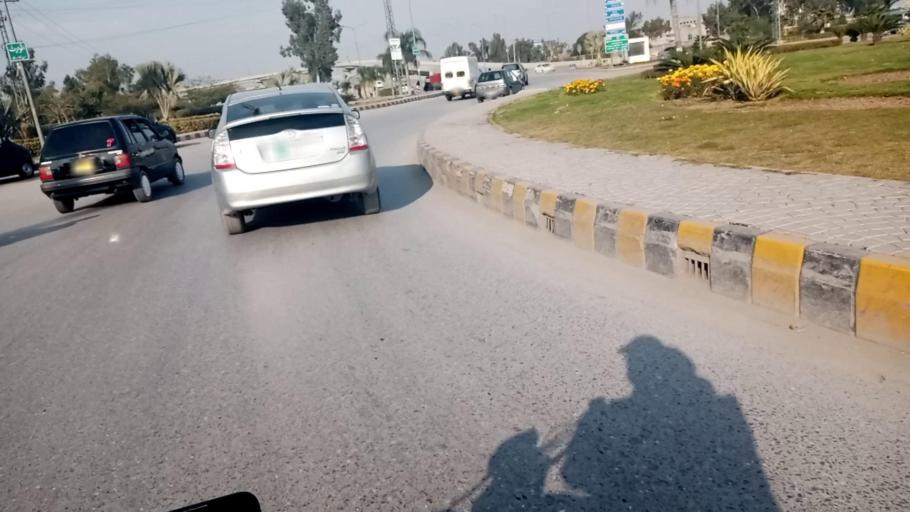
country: PK
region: Khyber Pakhtunkhwa
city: Peshawar
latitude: 33.9926
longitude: 71.4566
